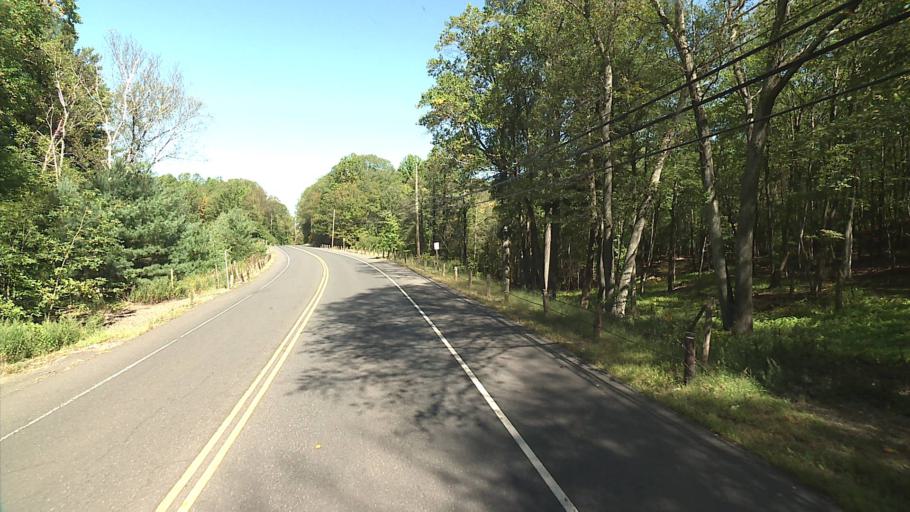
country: US
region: Connecticut
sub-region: New Haven County
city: Prospect
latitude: 41.5010
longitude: -72.9497
